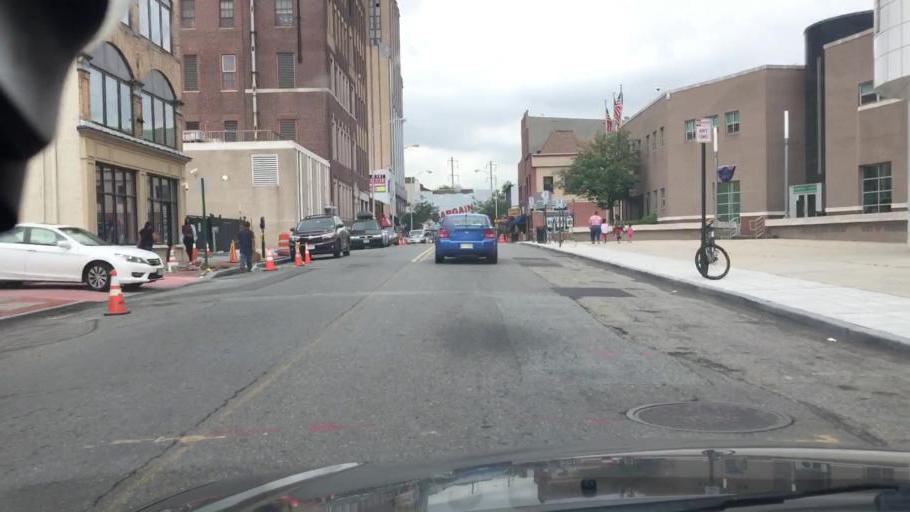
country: US
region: New Jersey
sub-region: Union County
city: Elizabeth
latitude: 40.6667
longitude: -74.2129
